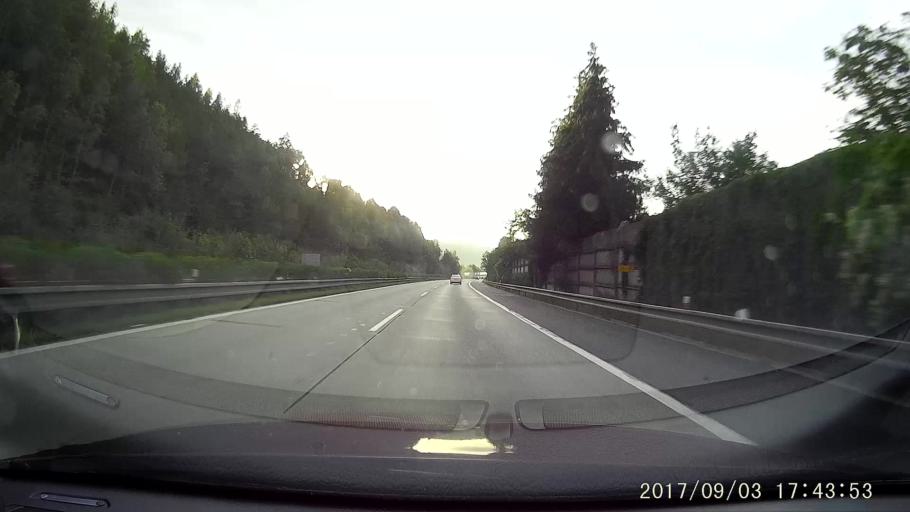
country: CZ
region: Central Bohemia
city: Ondrejov
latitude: 49.8708
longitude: 14.7720
